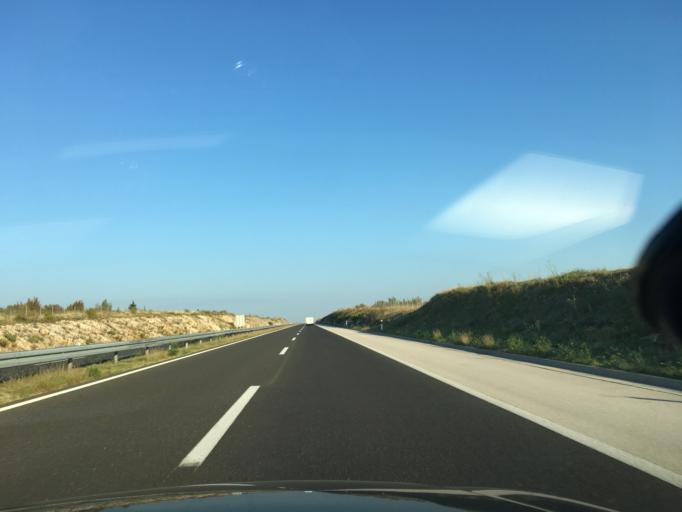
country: HR
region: Zadarska
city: Polaca
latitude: 44.0700
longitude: 15.5209
